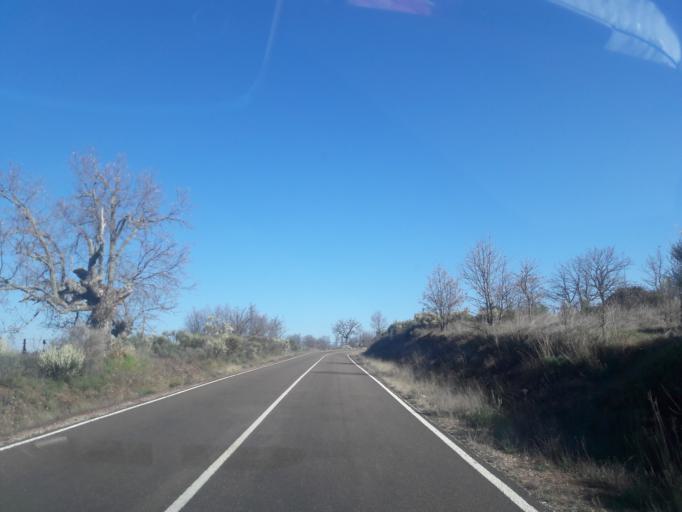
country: ES
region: Castille and Leon
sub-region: Provincia de Salamanca
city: Cabeza del Caballo
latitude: 41.1028
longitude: -6.5545
